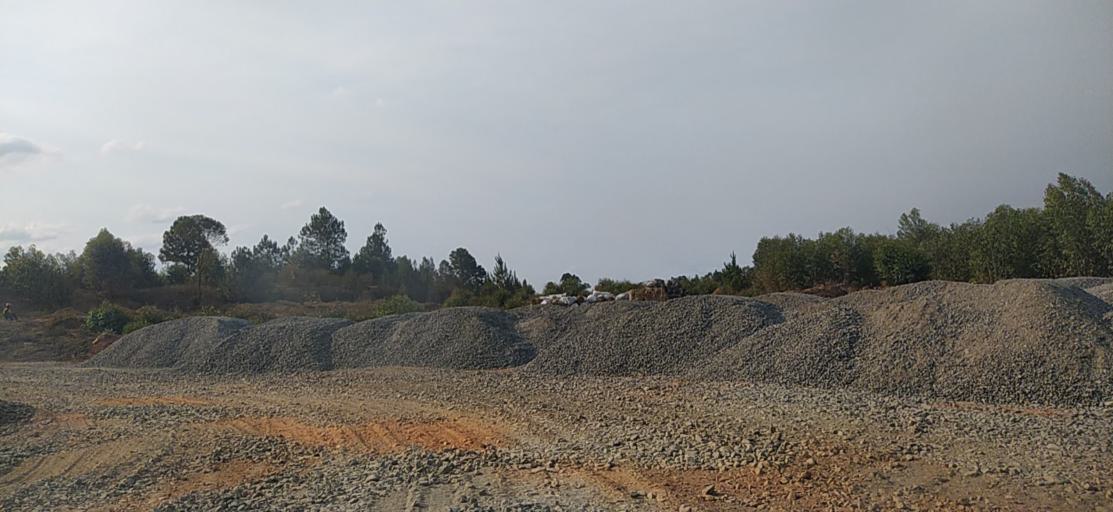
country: MG
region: Alaotra Mangoro
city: Moramanga
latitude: -18.6679
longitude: 48.2749
